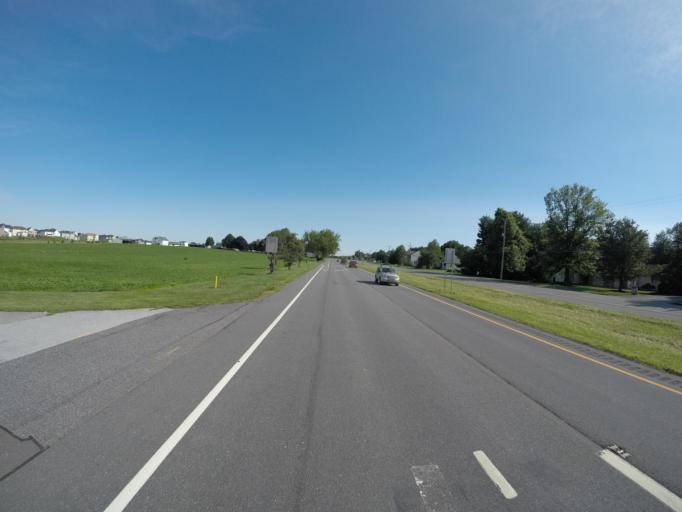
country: US
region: Delaware
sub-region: New Castle County
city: Delaware City
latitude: 39.5608
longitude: -75.6535
